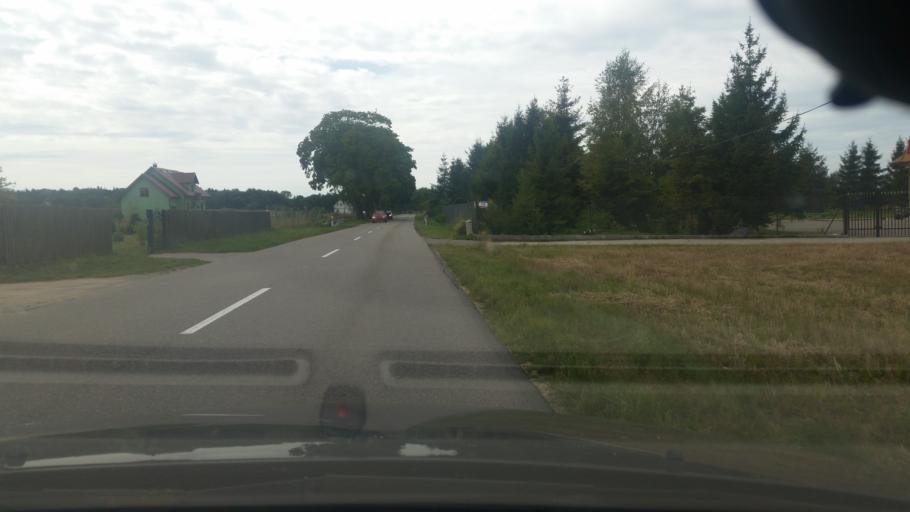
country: PL
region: Pomeranian Voivodeship
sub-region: Powiat leborski
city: Leba
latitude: 54.7348
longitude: 17.6310
